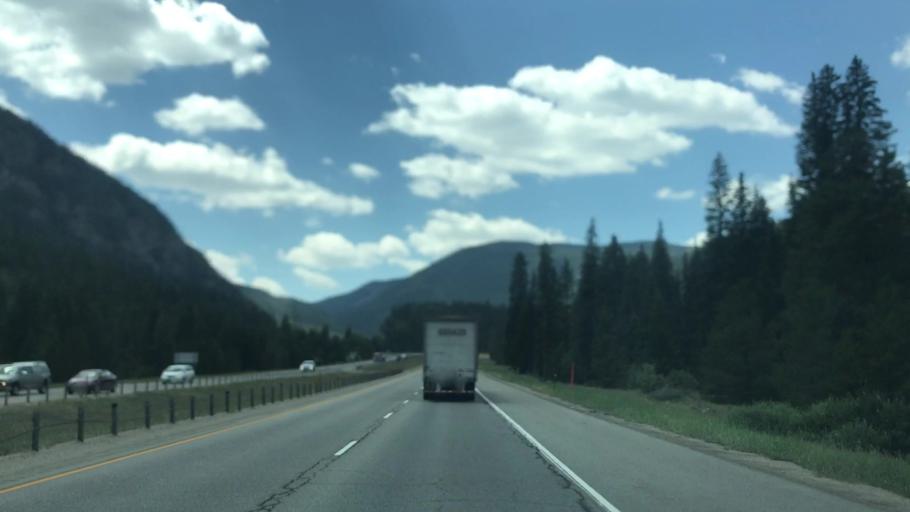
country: US
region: Colorado
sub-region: Summit County
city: Frisco
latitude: 39.5513
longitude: -106.1365
